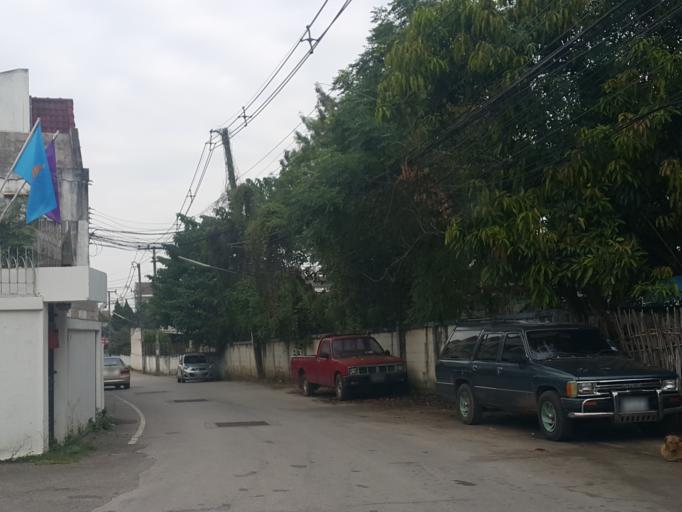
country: TH
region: Lampang
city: Lampang
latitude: 18.2899
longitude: 99.5131
